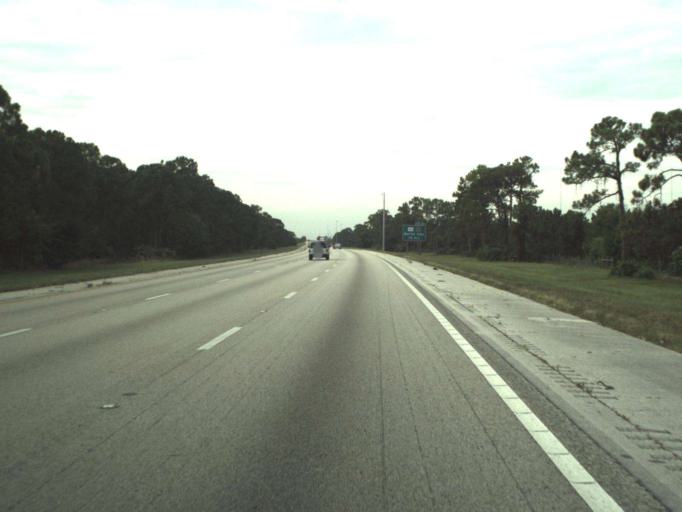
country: US
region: Florida
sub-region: Saint Lucie County
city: Port Saint Lucie
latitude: 27.1748
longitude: -80.3969
